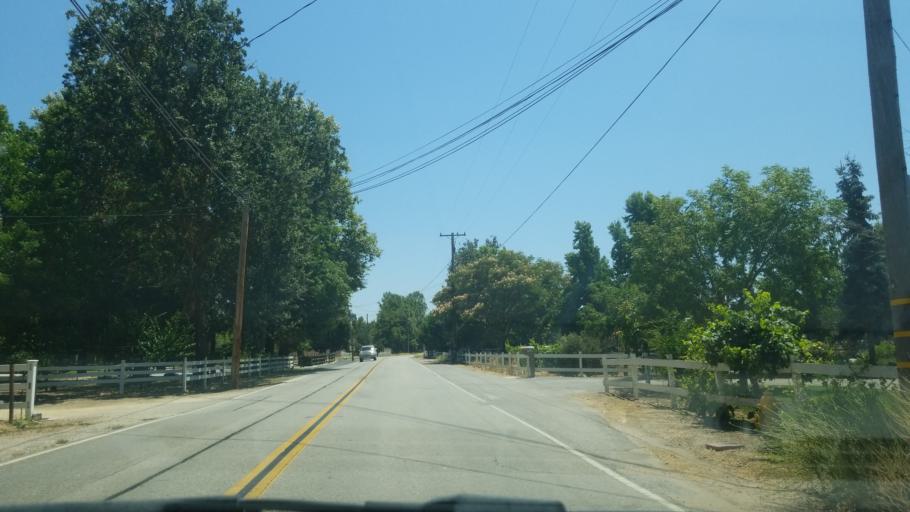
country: US
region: California
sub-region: San Luis Obispo County
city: Atascadero
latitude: 35.4961
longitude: -120.6491
